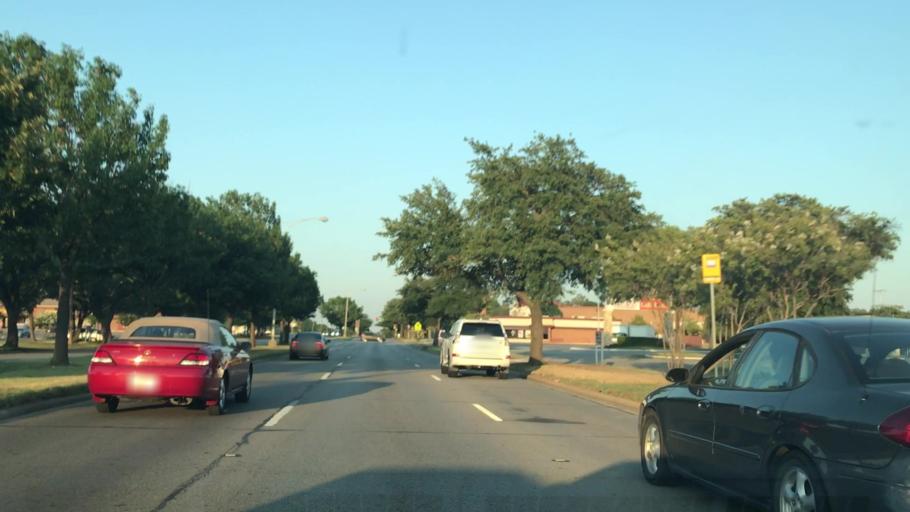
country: US
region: Texas
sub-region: Dallas County
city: Farmers Branch
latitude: 32.9095
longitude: -96.8544
